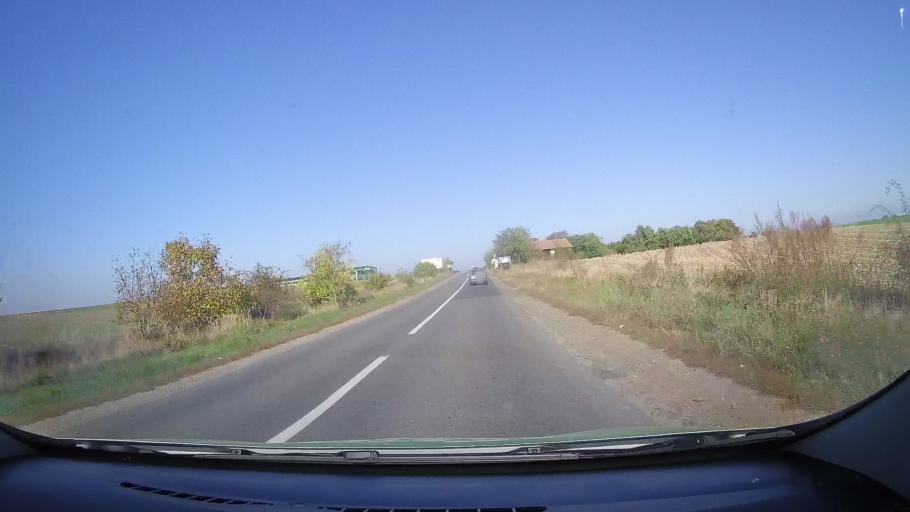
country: RO
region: Satu Mare
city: Carei
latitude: 47.6692
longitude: 22.4863
